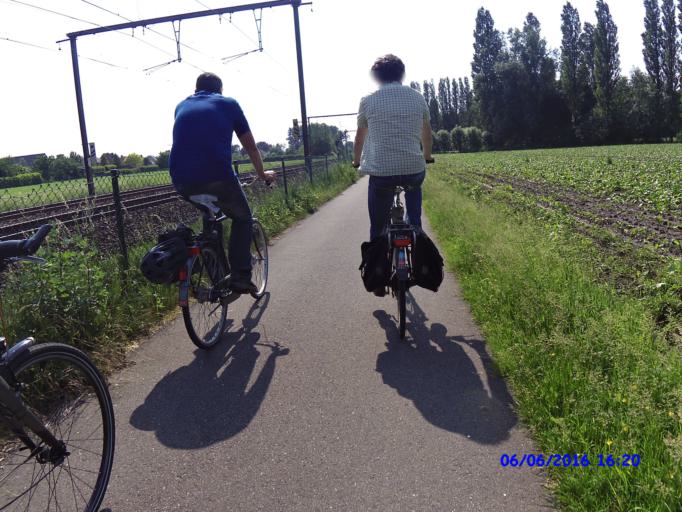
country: BE
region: Flanders
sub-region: Provincie Oost-Vlaanderen
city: Lokeren
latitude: 51.1019
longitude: 3.9640
